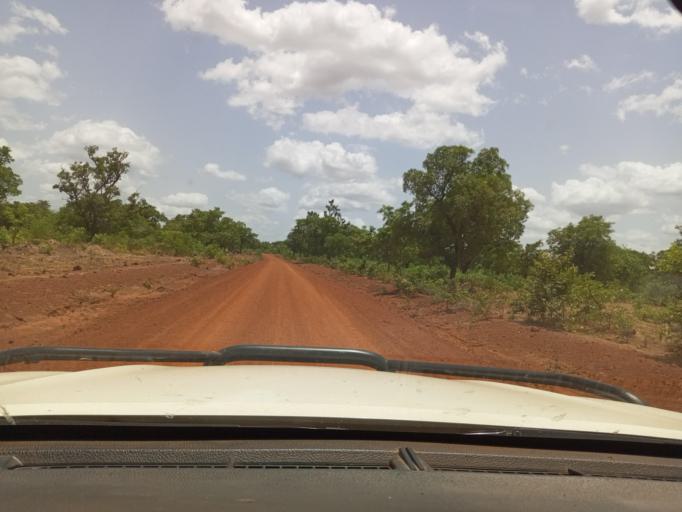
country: ML
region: Sikasso
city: Kolondieba
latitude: 11.7198
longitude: -6.8095
